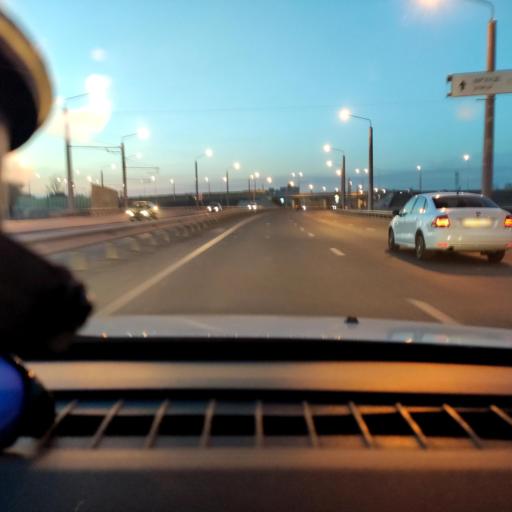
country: RU
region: Samara
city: Samara
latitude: 53.1631
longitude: 50.0872
